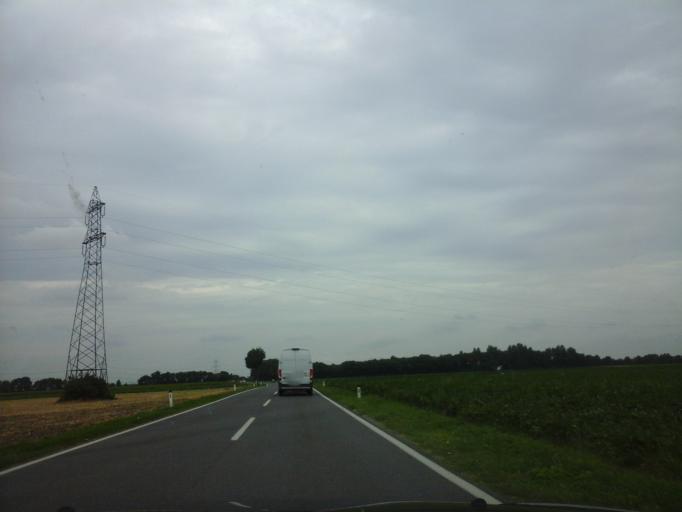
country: AT
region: Lower Austria
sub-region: Politischer Bezirk Ganserndorf
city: Mannsdorf an der Donau
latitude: 48.1546
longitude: 16.6558
